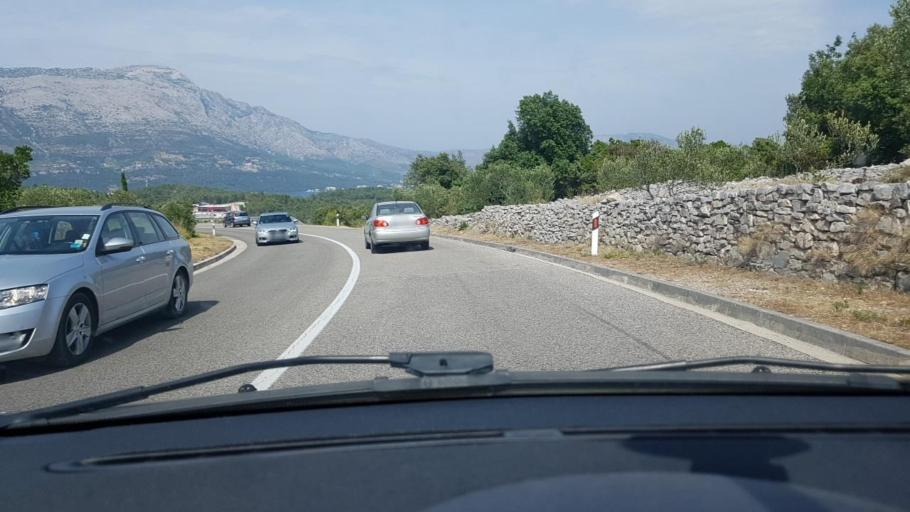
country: HR
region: Dubrovacko-Neretvanska
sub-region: Grad Korcula
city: Zrnovo
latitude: 42.9452
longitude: 17.1192
